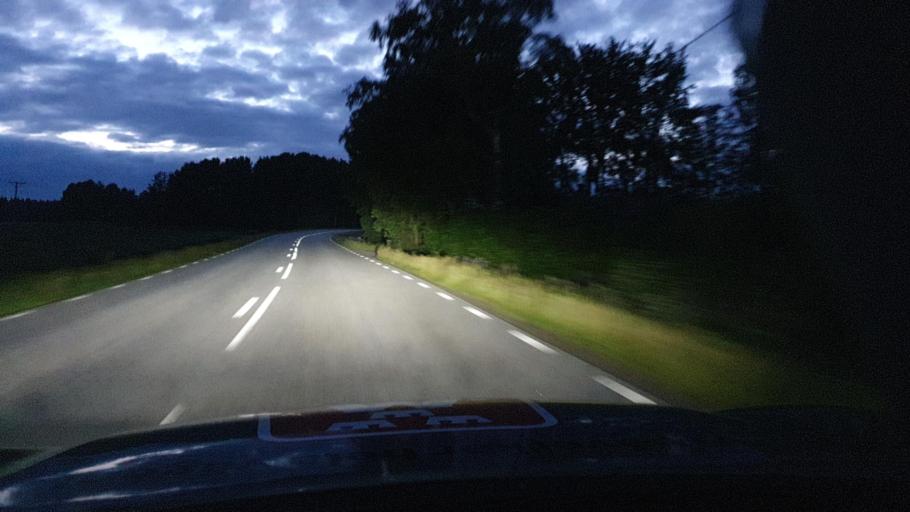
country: SE
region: OErebro
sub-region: Karlskoga Kommun
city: Karlskoga
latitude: 59.3935
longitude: 14.5105
